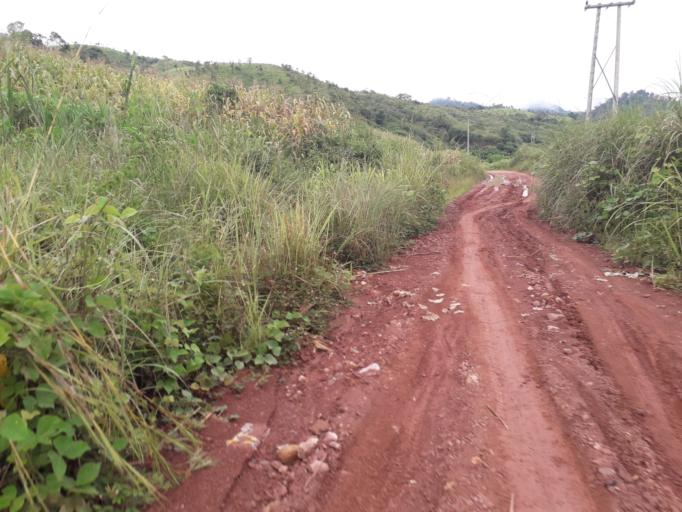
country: CN
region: Yunnan
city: Menglie
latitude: 22.2587
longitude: 101.5936
